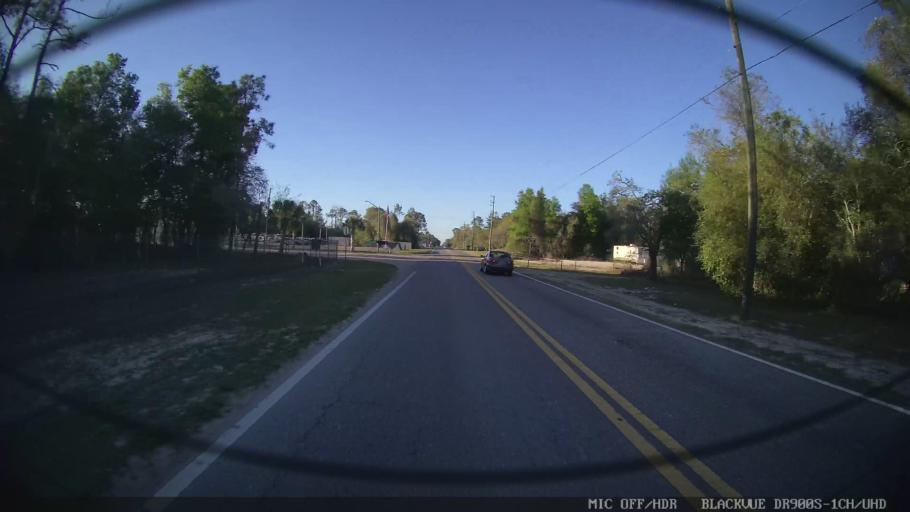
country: US
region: Florida
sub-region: Pasco County
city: Shady Hills
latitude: 28.3814
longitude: -82.5512
